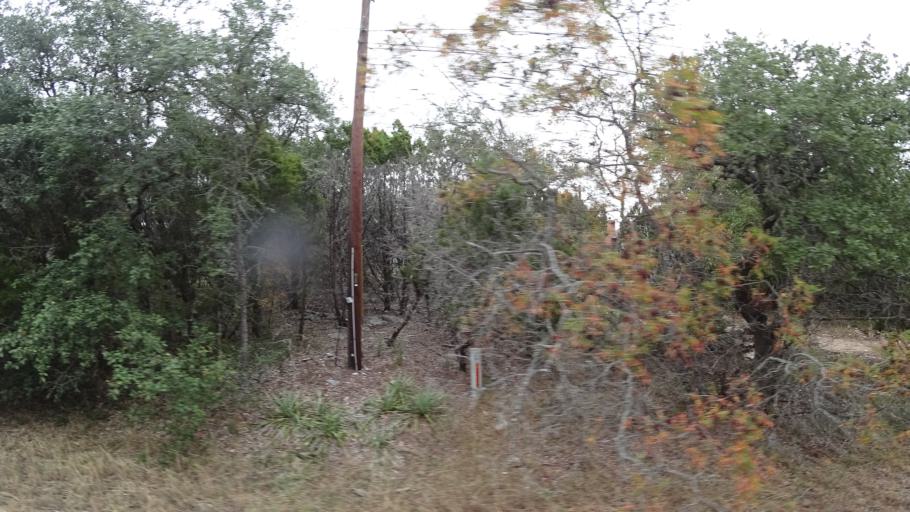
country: US
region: Texas
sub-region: Williamson County
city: Anderson Mill
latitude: 30.4513
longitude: -97.8412
